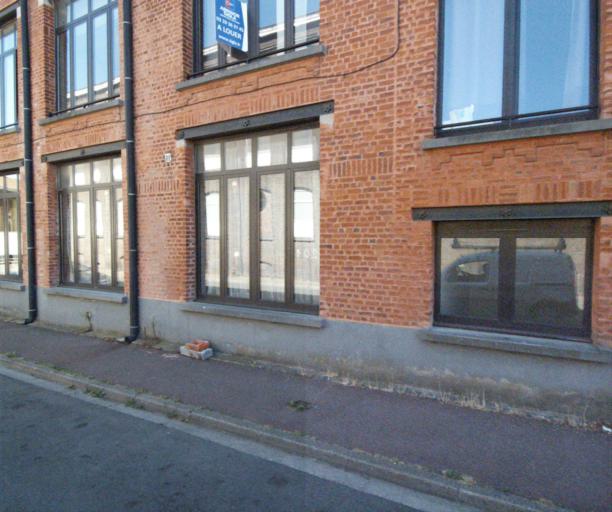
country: FR
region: Nord-Pas-de-Calais
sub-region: Departement du Nord
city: Tourcoing
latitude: 50.7220
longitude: 3.1755
